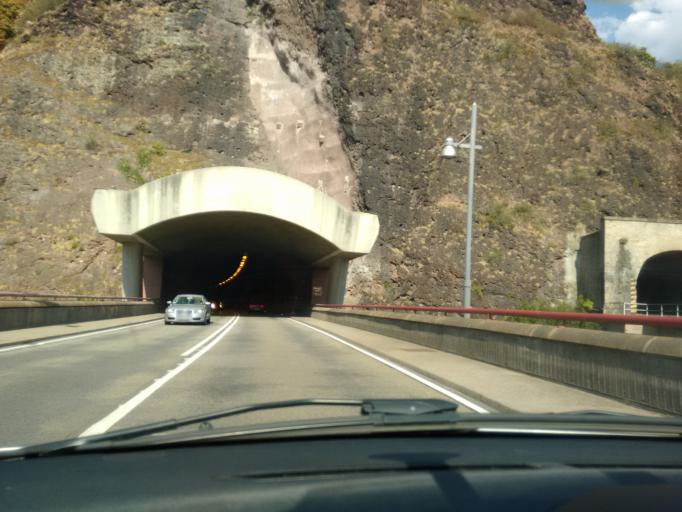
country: DE
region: Rheinland-Pfalz
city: Hintertiefenbach
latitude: 49.7043
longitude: 7.3469
